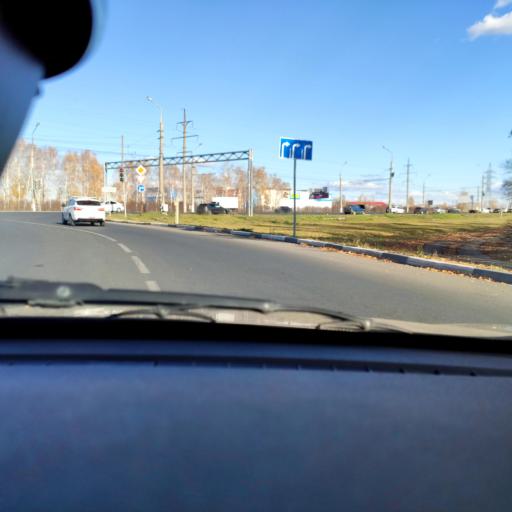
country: RU
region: Samara
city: Tol'yatti
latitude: 53.5453
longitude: 49.3738
